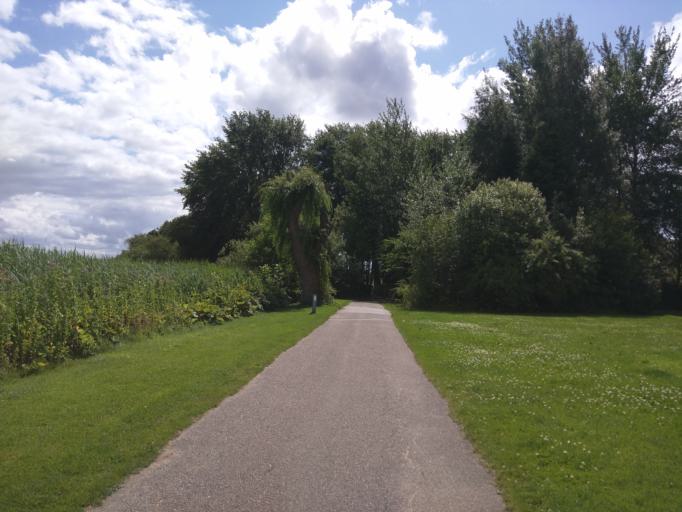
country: DK
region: Central Jutland
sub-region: Viborg Kommune
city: Viborg
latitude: 56.4397
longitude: 9.4042
